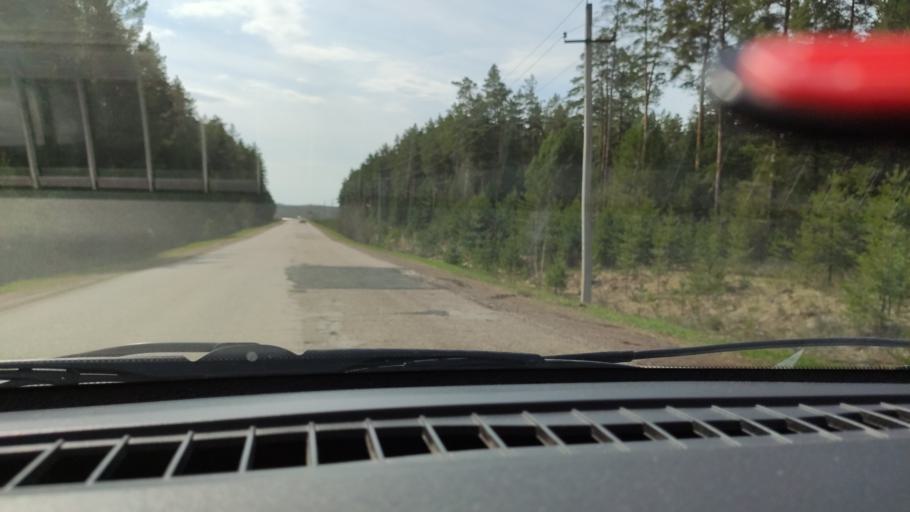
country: RU
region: Bashkortostan
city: Dyurtyuli
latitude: 55.5048
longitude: 54.8975
